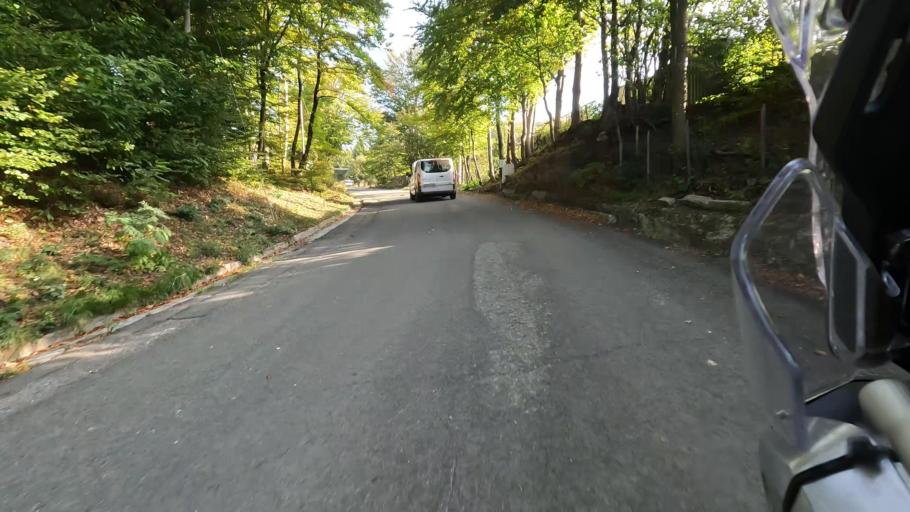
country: IT
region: Liguria
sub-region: Provincia di Savona
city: Urbe
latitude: 44.4592
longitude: 8.5802
